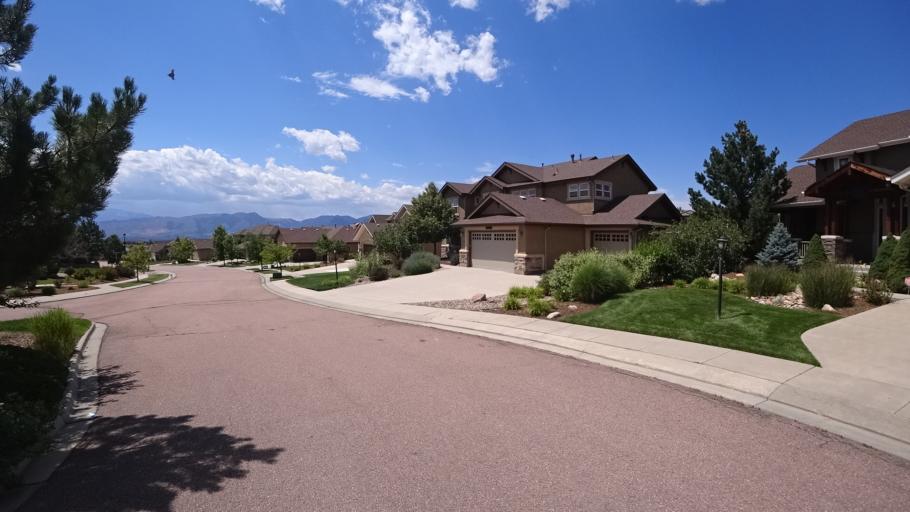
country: US
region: Colorado
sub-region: El Paso County
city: Black Forest
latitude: 38.9720
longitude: -104.7603
